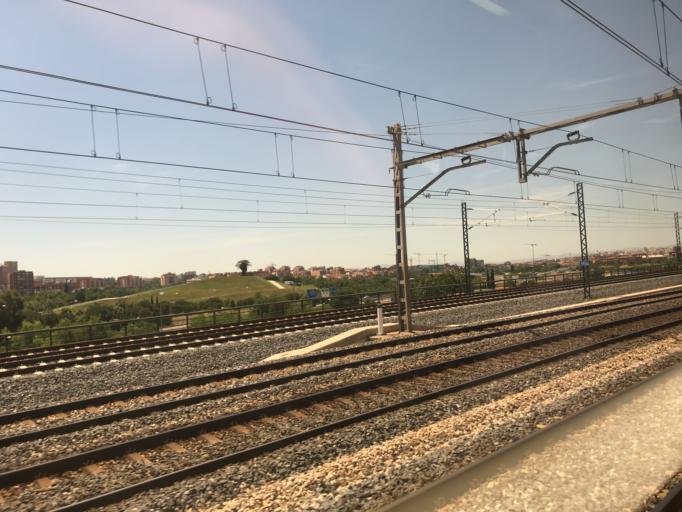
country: ES
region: Madrid
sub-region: Provincia de Madrid
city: Usera
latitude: 40.3761
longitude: -3.6819
